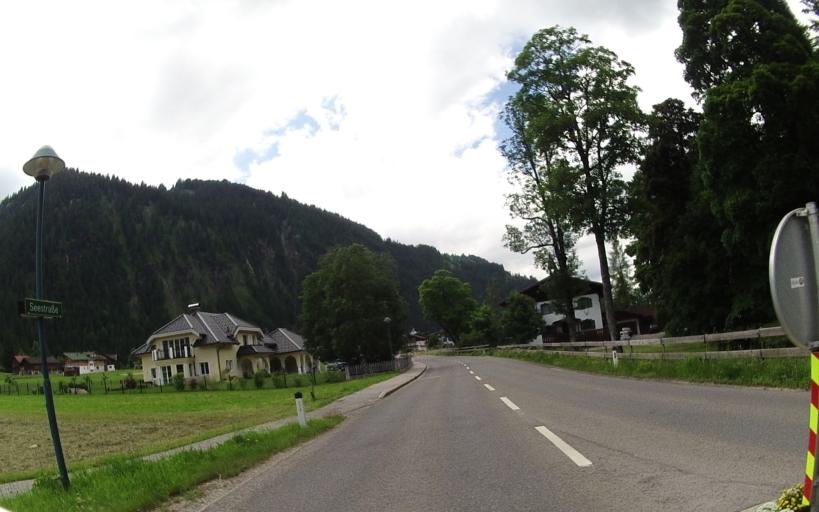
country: AT
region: Tyrol
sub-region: Politischer Bezirk Reutte
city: Graen
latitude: 47.4925
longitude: 10.5653
